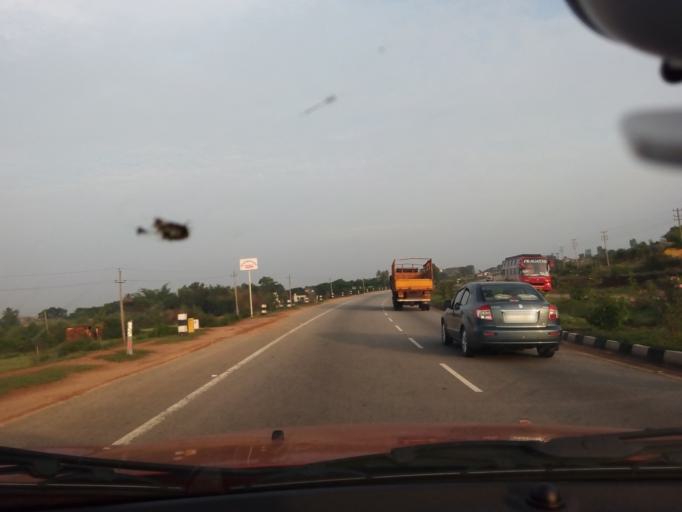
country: IN
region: Karnataka
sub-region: Bangalore Rural
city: Nelamangala
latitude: 13.0619
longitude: 77.2945
